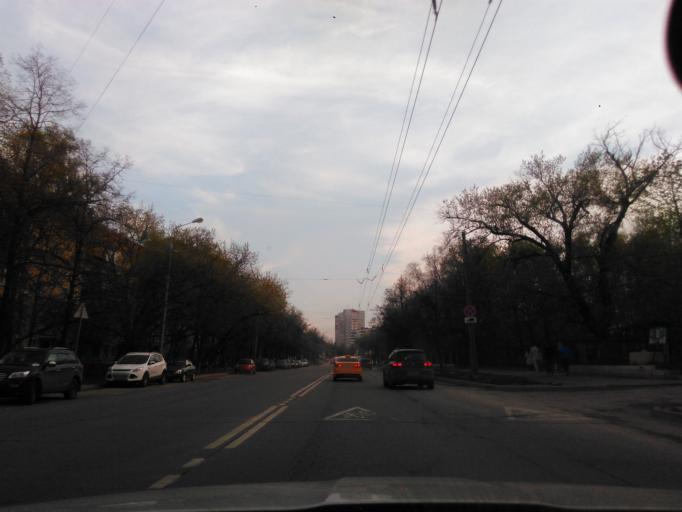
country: RU
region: Moscow
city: Lyublino
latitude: 55.6862
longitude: 37.7519
